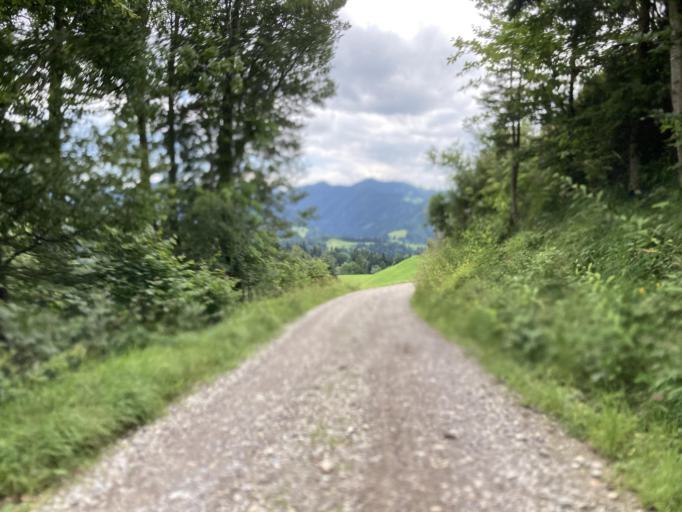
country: CH
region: Thurgau
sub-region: Muenchwilen District
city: Fischingen
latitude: 47.3662
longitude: 8.9419
